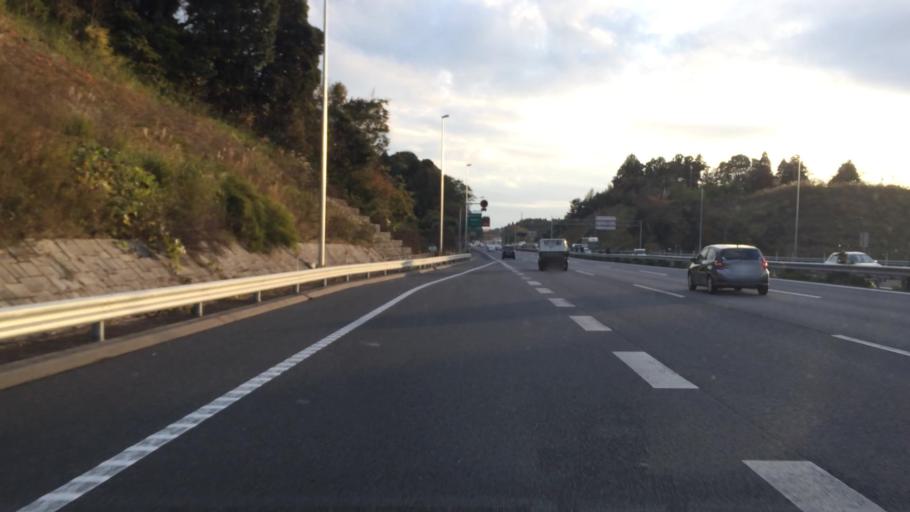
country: JP
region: Chiba
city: Shisui
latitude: 35.7234
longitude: 140.2914
